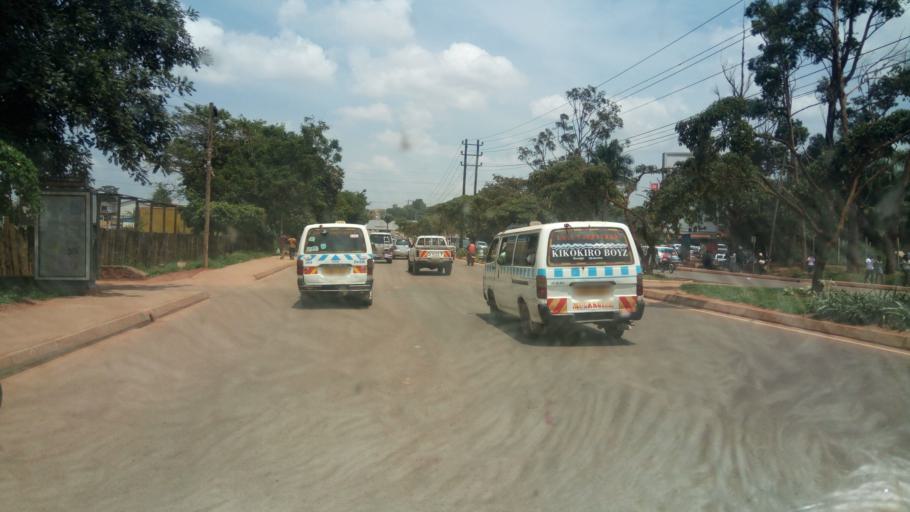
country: UG
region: Central Region
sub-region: Kampala District
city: Kampala
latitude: 0.3259
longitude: 32.6089
